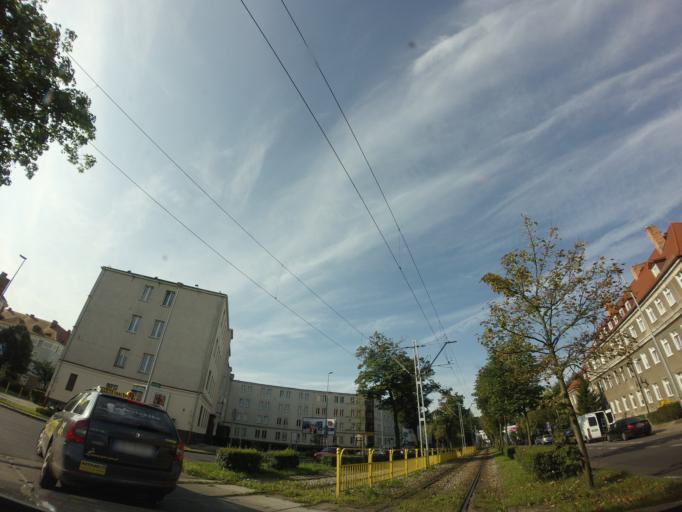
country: PL
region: West Pomeranian Voivodeship
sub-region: Szczecin
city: Szczecin
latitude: 53.4231
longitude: 14.5309
